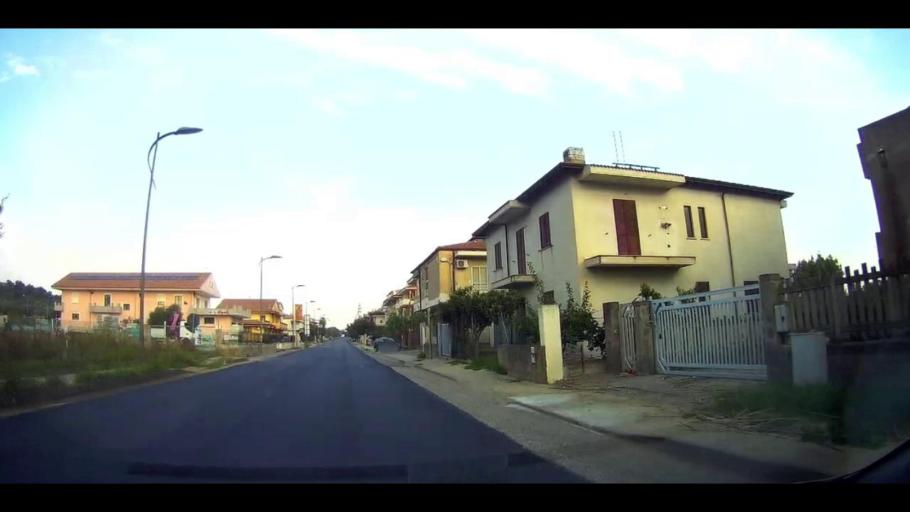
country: IT
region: Calabria
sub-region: Provincia di Crotone
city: Torretta
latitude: 39.4564
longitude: 17.0332
